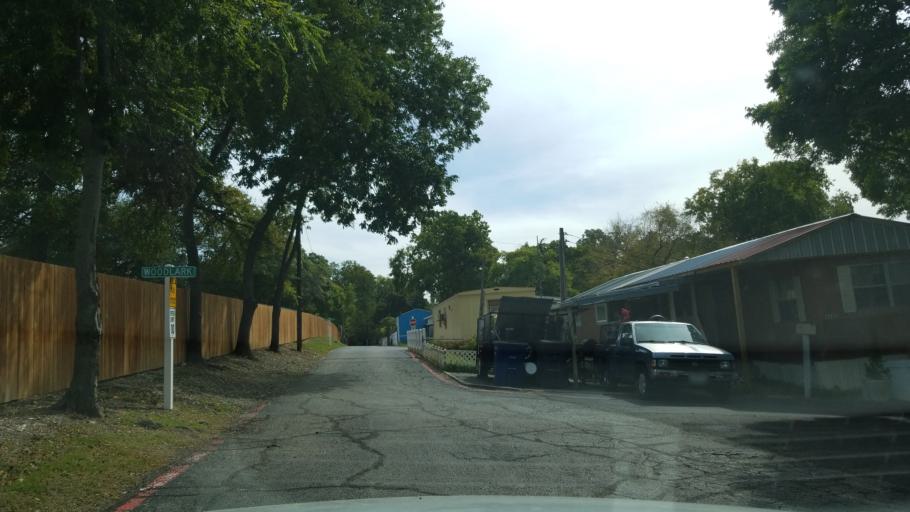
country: US
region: Texas
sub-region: Dallas County
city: Highland Park
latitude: 32.7889
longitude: -96.7233
